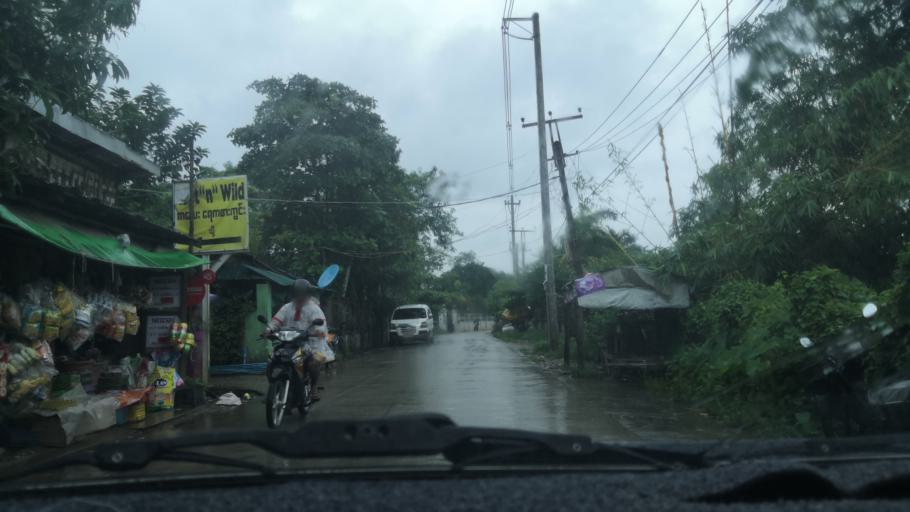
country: MM
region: Yangon
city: Yangon
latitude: 16.8813
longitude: 96.1486
